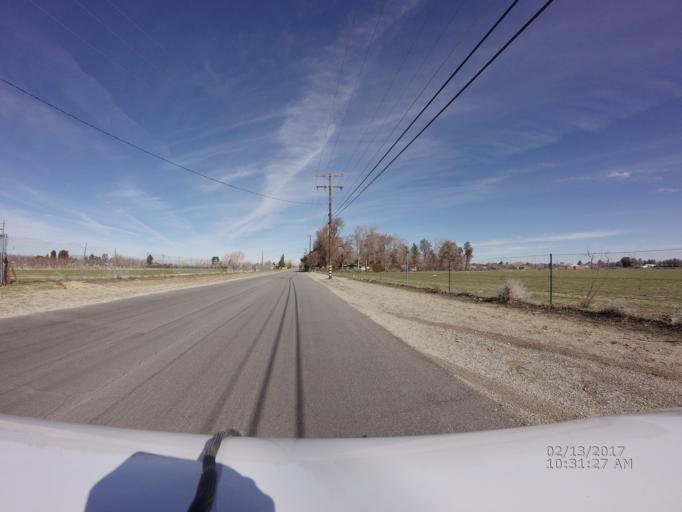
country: US
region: California
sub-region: Los Angeles County
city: Littlerock
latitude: 34.5329
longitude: -117.9793
